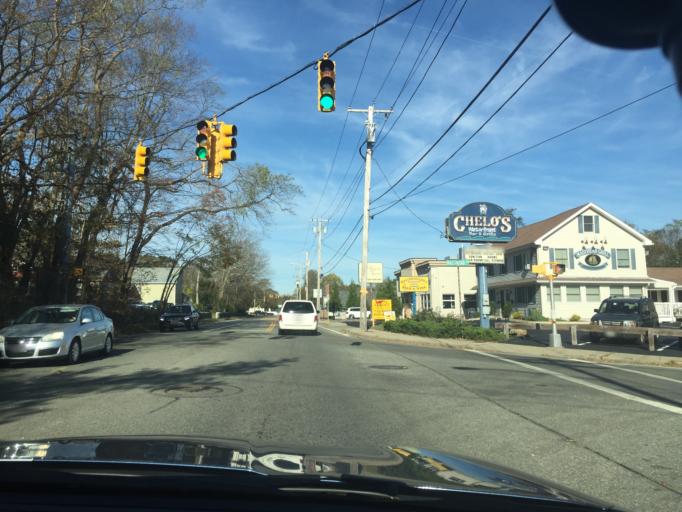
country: US
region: Rhode Island
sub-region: Kent County
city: East Greenwich
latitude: 41.6844
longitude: -71.4524
